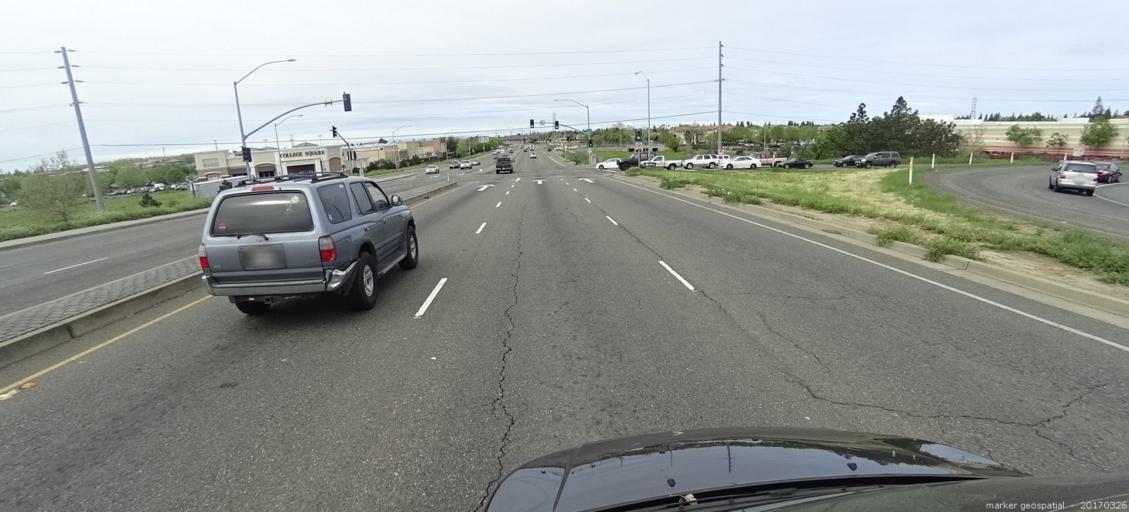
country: US
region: California
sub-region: Sacramento County
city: Laguna
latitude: 38.4570
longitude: -121.4120
